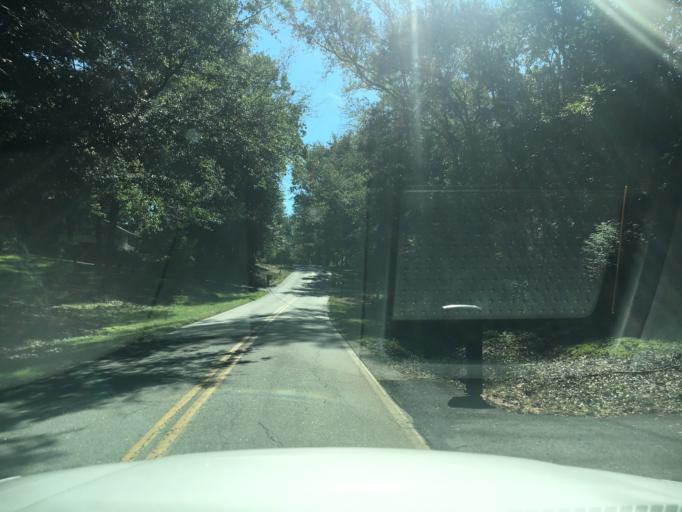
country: US
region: South Carolina
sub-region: Greenville County
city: Taylors
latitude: 34.9022
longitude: -82.2760
